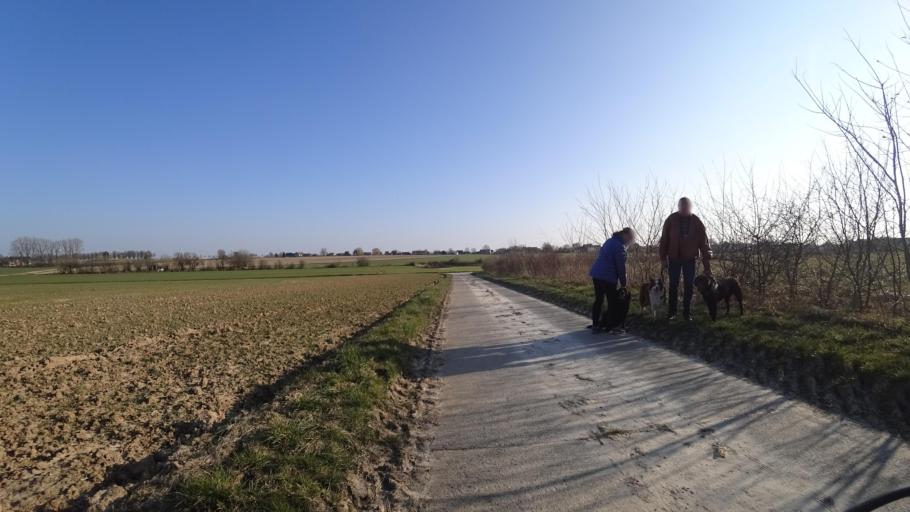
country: BE
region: Wallonia
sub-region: Province du Brabant Wallon
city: Chastre-Villeroux-Blanmont
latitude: 50.6156
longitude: 4.6564
